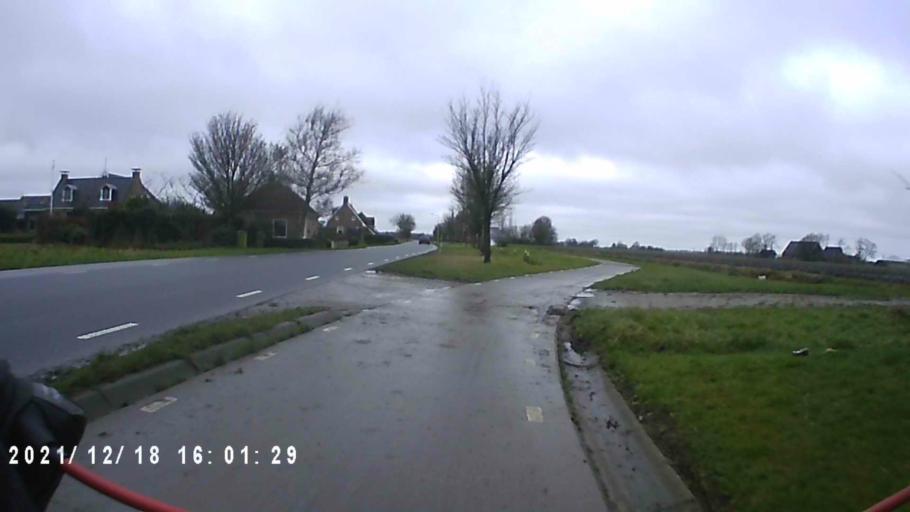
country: NL
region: Friesland
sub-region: Gemeente Dongeradeel
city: Anjum
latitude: 53.3449
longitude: 6.0857
